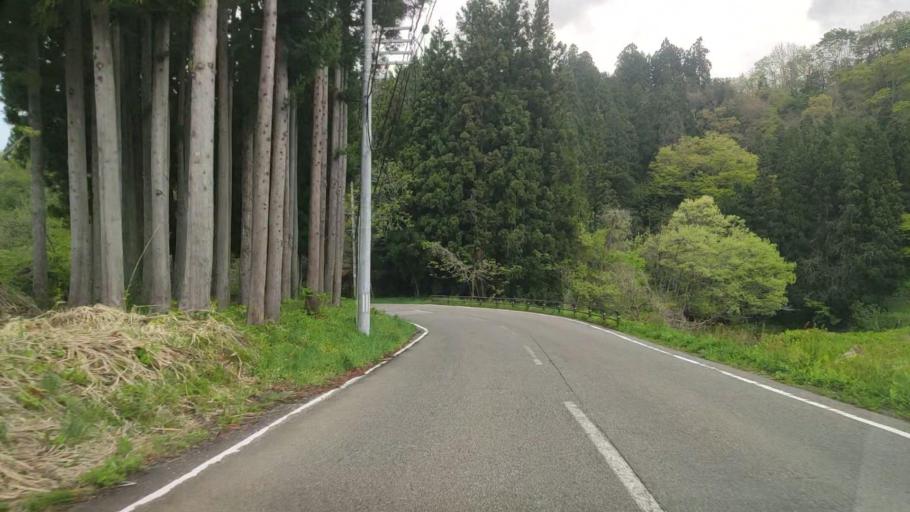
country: JP
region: Fukushima
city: Kitakata
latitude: 37.6579
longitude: 139.5903
